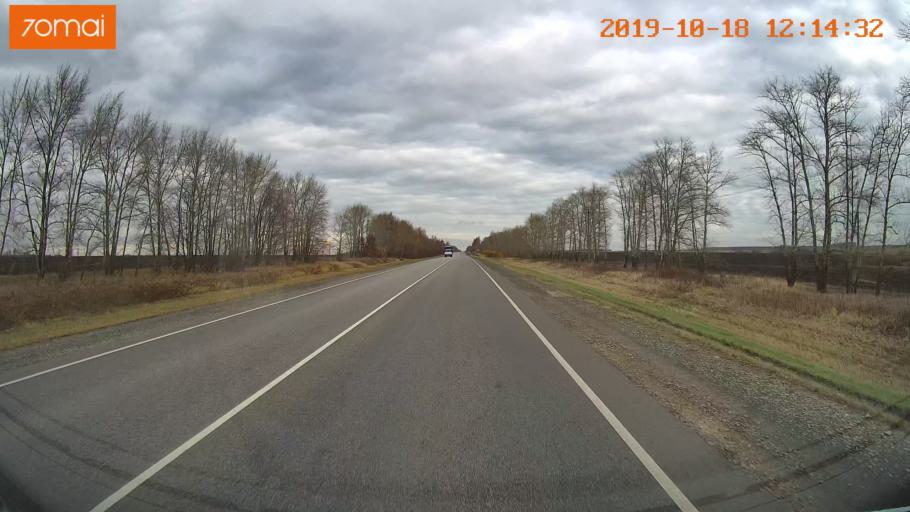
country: RU
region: Rjazan
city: Zakharovo
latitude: 54.4319
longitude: 39.3848
